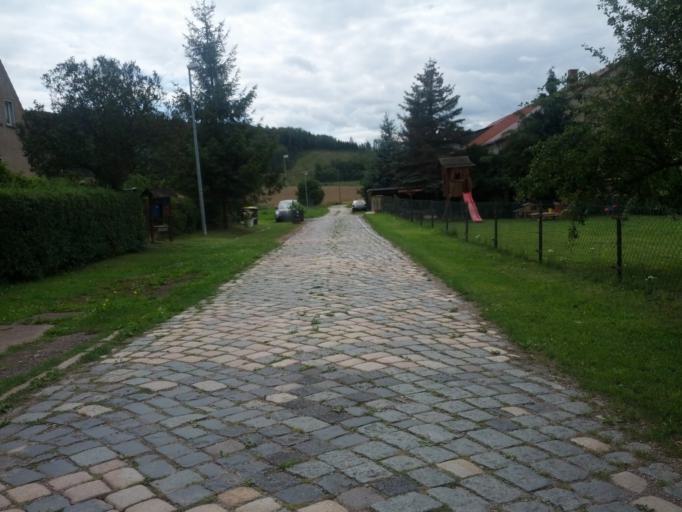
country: DE
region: Thuringia
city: Krauthausen
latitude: 51.0147
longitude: 10.2873
